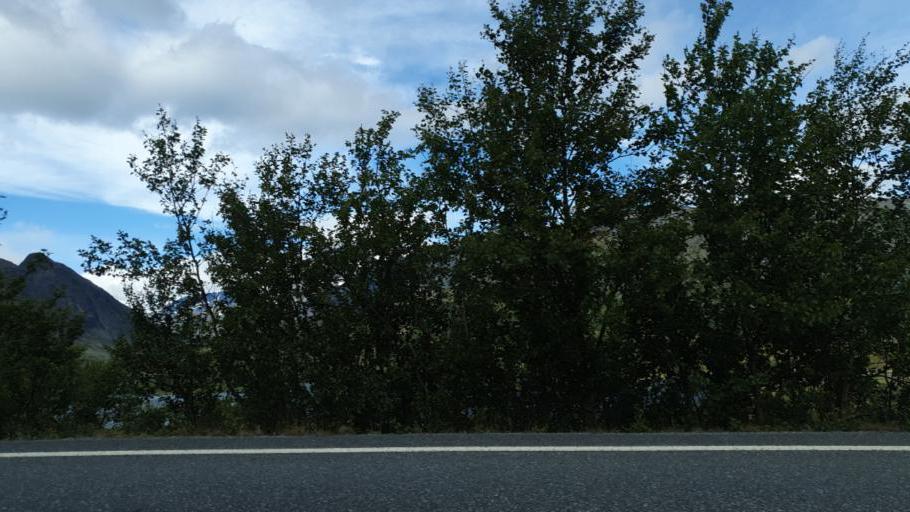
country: NO
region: Oppland
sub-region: Oystre Slidre
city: Heggenes
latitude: 61.4732
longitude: 8.8185
